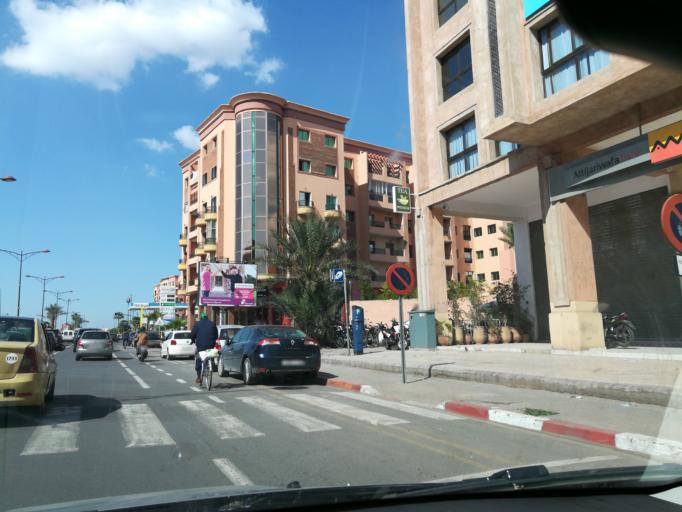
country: MA
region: Marrakech-Tensift-Al Haouz
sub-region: Marrakech
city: Marrakesh
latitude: 31.6526
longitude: -8.0196
